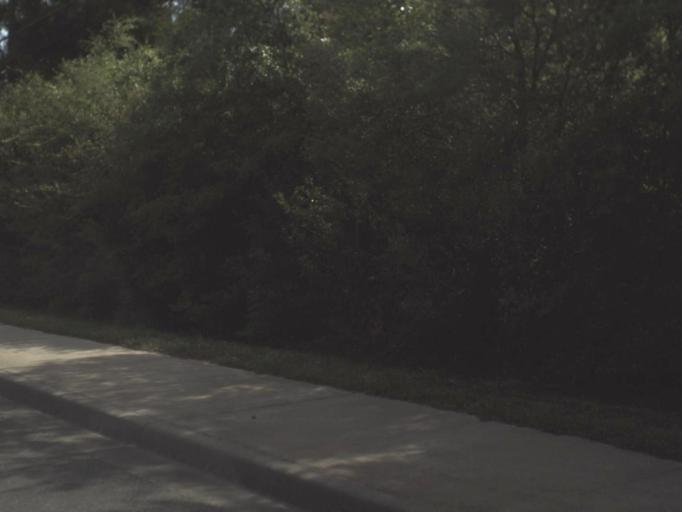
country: US
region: Florida
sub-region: Santa Rosa County
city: East Milton
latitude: 30.6261
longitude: -86.9672
